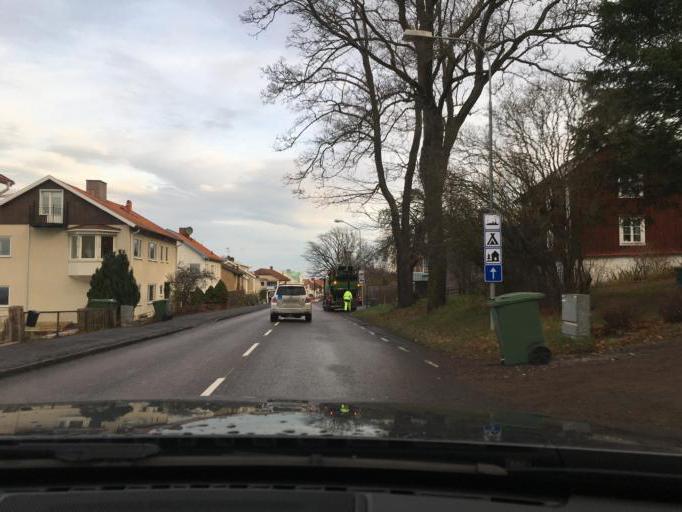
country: SE
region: Joenkoeping
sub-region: Jonkopings Kommun
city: Graenna
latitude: 58.0170
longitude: 14.4613
